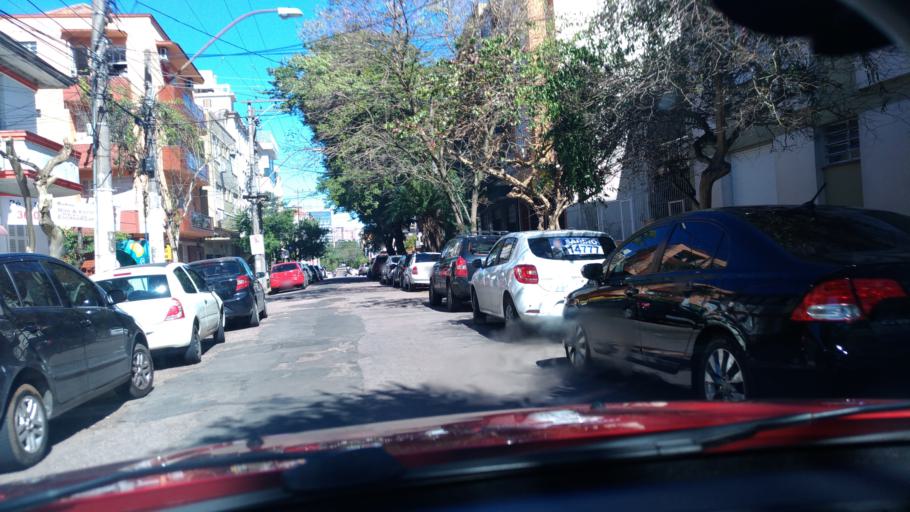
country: BR
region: Rio Grande do Sul
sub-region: Porto Alegre
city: Porto Alegre
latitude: -30.0392
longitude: -51.2093
